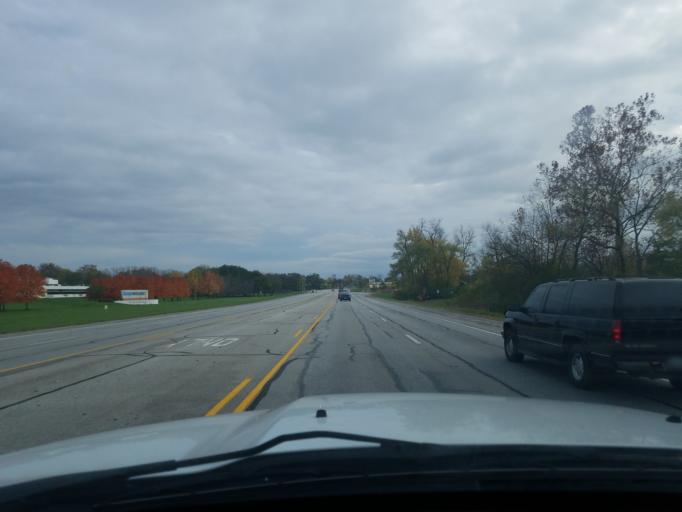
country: US
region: Indiana
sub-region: Shelby County
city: Shelbyville
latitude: 39.5363
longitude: -85.7763
